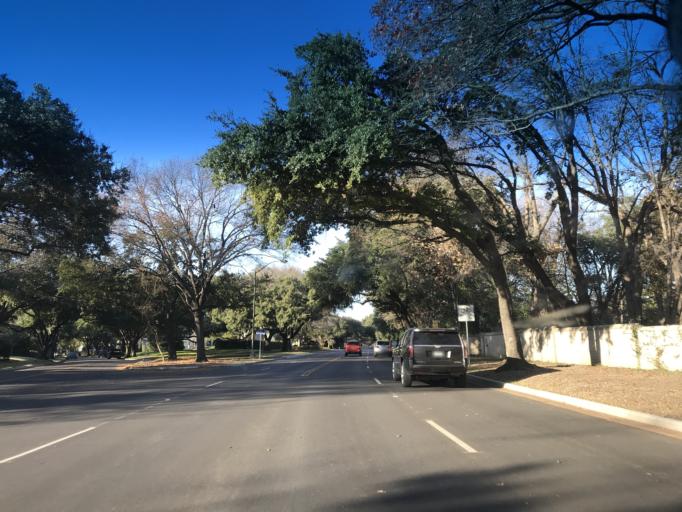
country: US
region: Texas
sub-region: Dallas County
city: Highland Park
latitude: 32.8245
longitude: -96.8032
